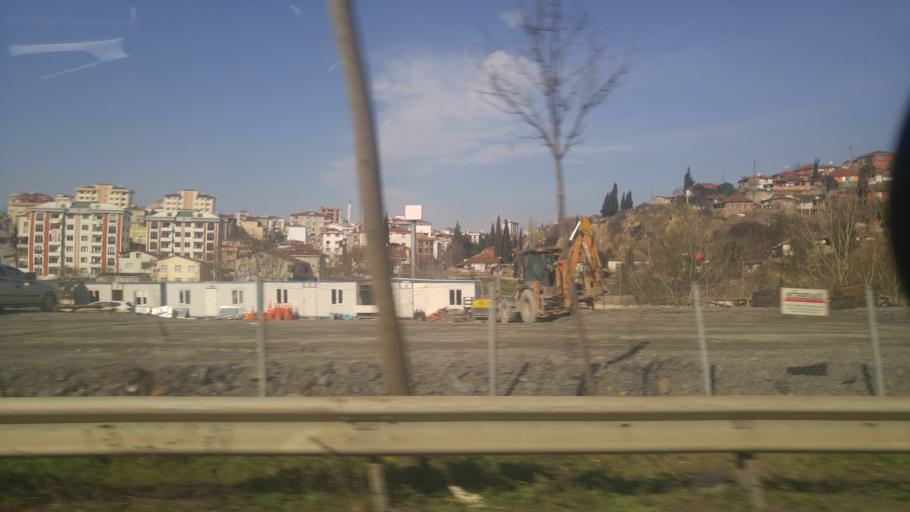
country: TR
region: Kocaeli
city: Darica
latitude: 40.8320
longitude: 29.3686
